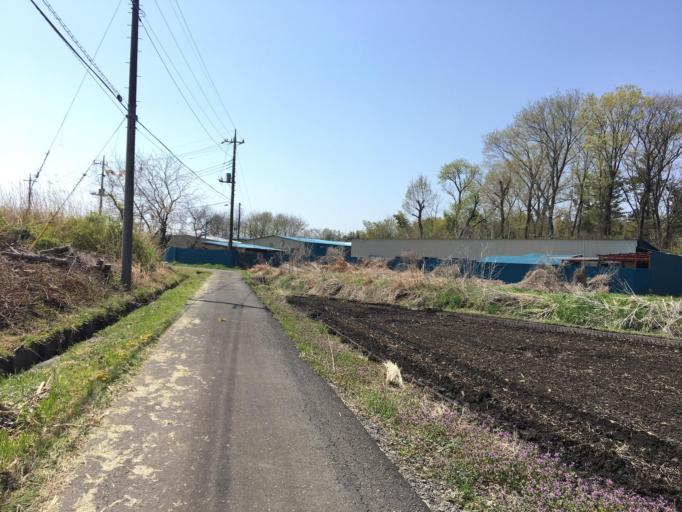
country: JP
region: Saitama
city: Sakado
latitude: 35.9487
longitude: 139.3485
